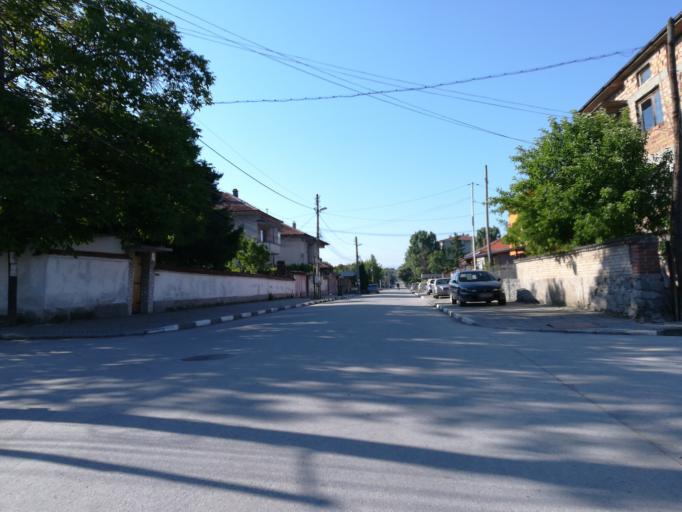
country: BG
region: Stara Zagora
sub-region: Obshtina Chirpan
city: Chirpan
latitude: 42.1067
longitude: 25.2242
